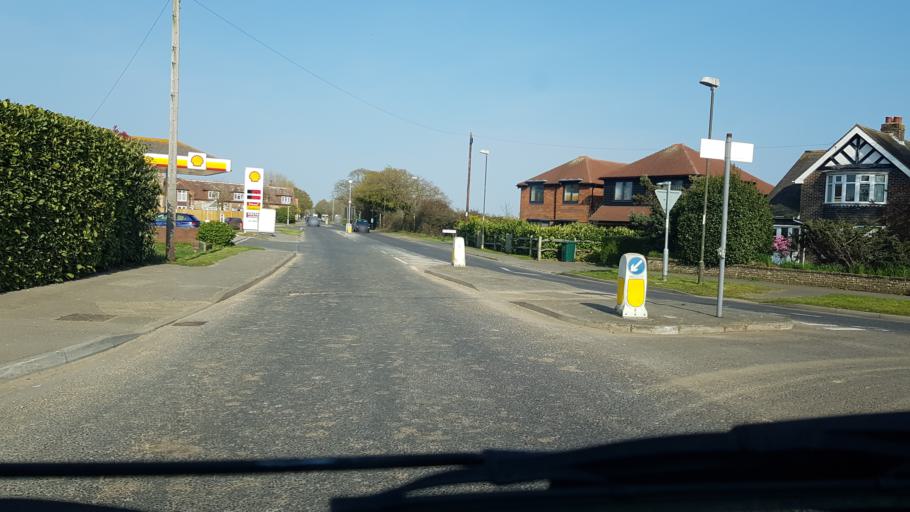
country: GB
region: England
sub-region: West Sussex
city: Birdham
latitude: 50.7891
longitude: -0.8396
